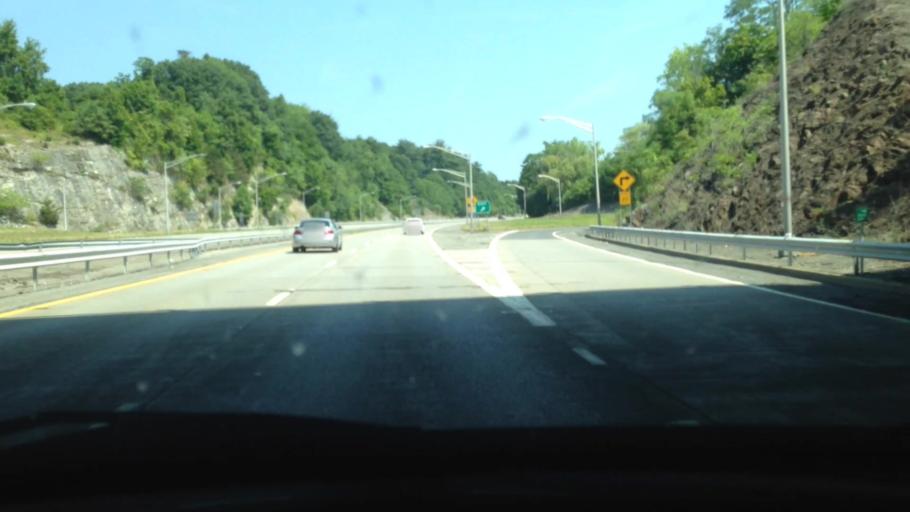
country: US
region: New York
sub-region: Ulster County
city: Kingston
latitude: 41.9268
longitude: -73.9858
